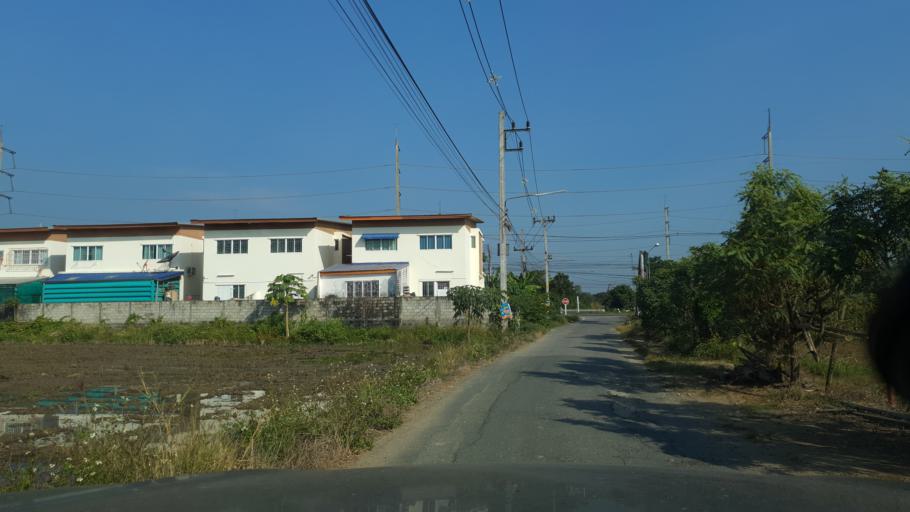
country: TH
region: Chiang Mai
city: Saraphi
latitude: 18.7190
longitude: 98.9938
